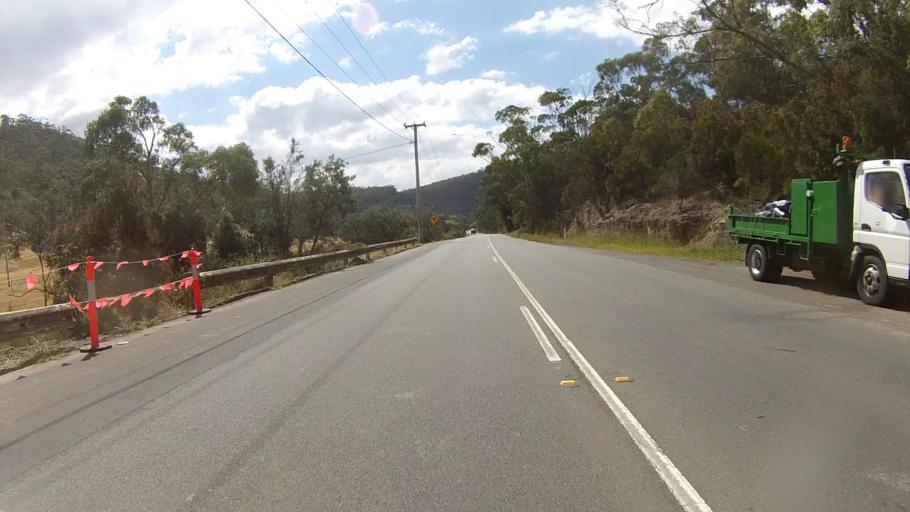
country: AU
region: Tasmania
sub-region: Clarence
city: Cambridge
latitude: -42.8444
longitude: 147.4200
